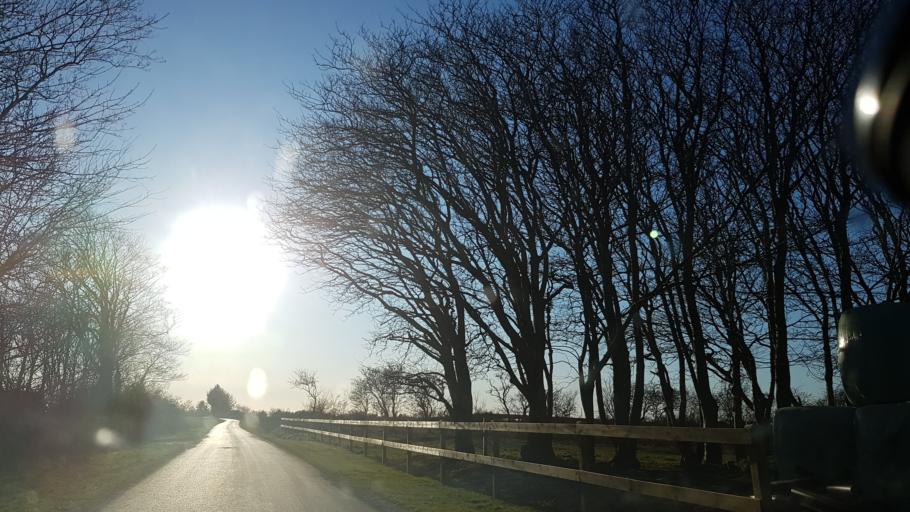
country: DK
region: South Denmark
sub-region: Esbjerg Kommune
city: Bramming
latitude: 55.4217
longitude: 8.6570
